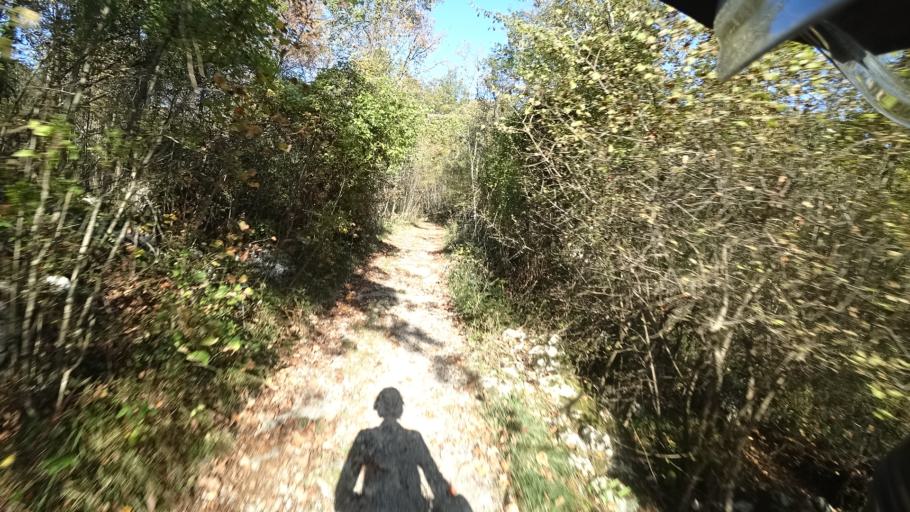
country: HR
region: Primorsko-Goranska
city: Kastav
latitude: 45.3993
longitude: 14.3258
